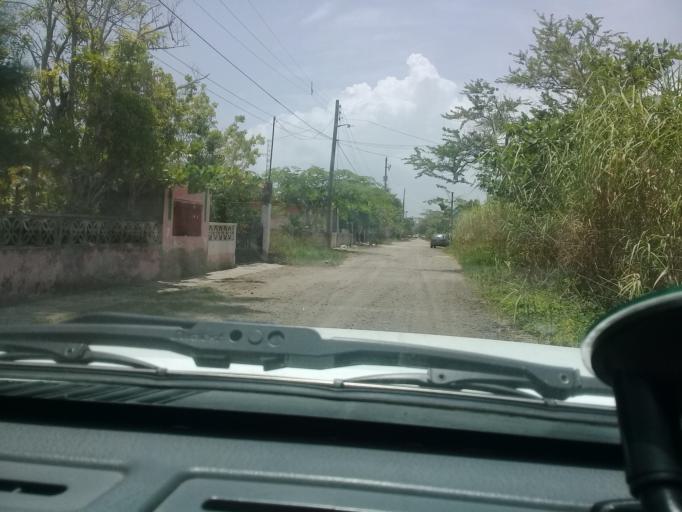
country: MX
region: Veracruz
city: Anahuac
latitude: 22.2273
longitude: -97.8187
